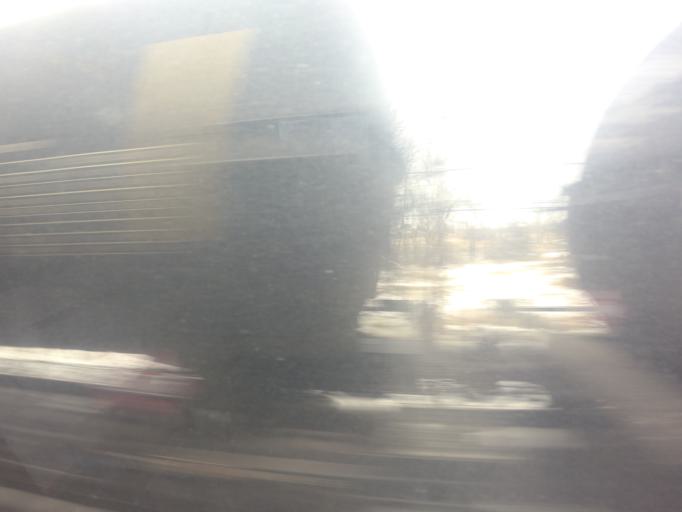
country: CA
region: Ontario
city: Quinte West
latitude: 44.1361
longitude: -77.5445
